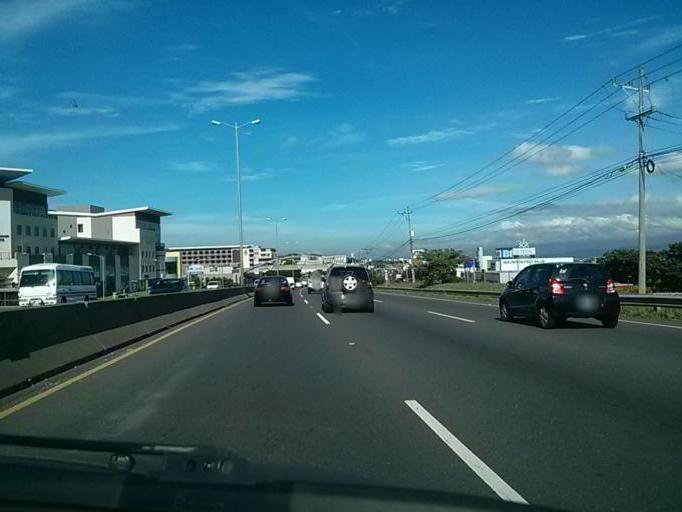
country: CR
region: San Jose
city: San Rafael
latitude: 9.9396
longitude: -84.1415
